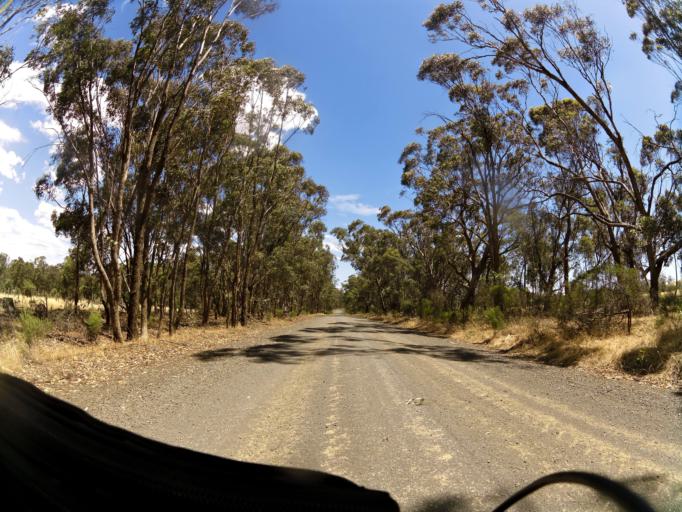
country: AU
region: Victoria
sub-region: Campaspe
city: Kyabram
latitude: -36.7981
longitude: 145.0795
